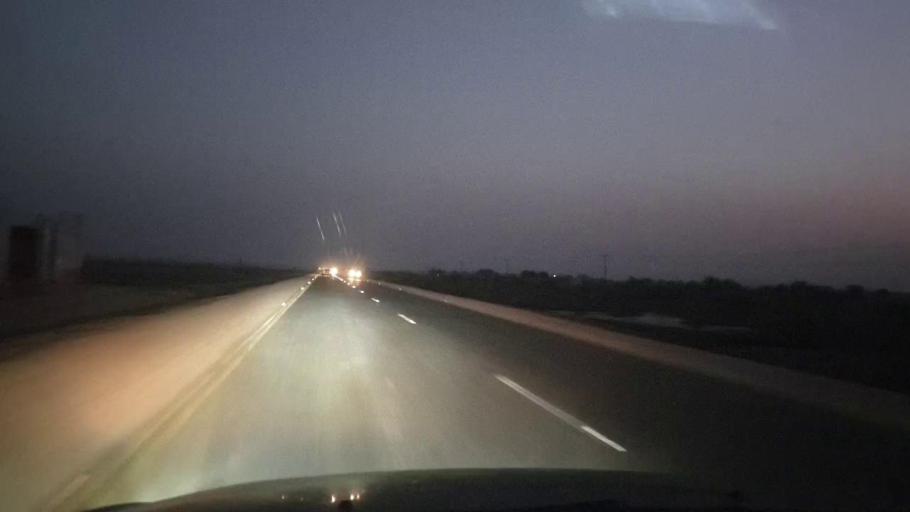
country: PK
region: Sindh
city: Chambar
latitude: 25.3414
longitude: 68.7940
